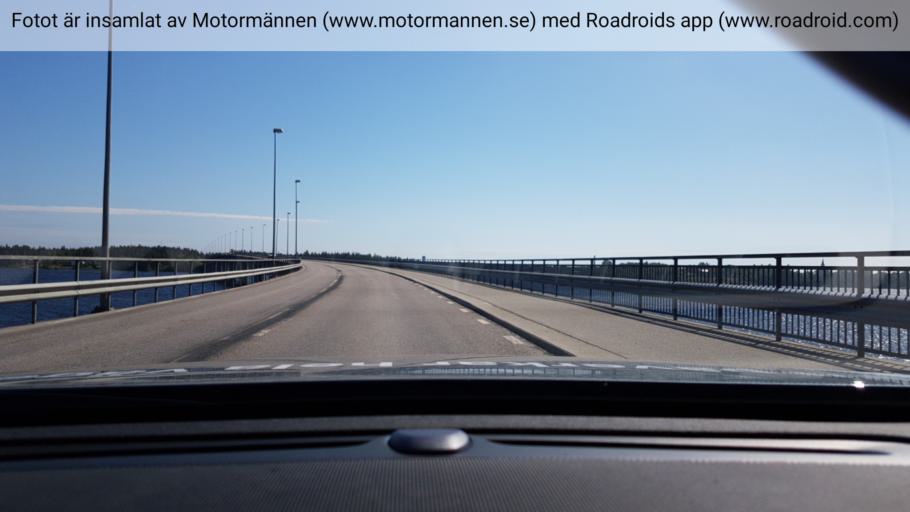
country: SE
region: Vaesterbotten
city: Obbola
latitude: 63.7103
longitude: 20.3275
